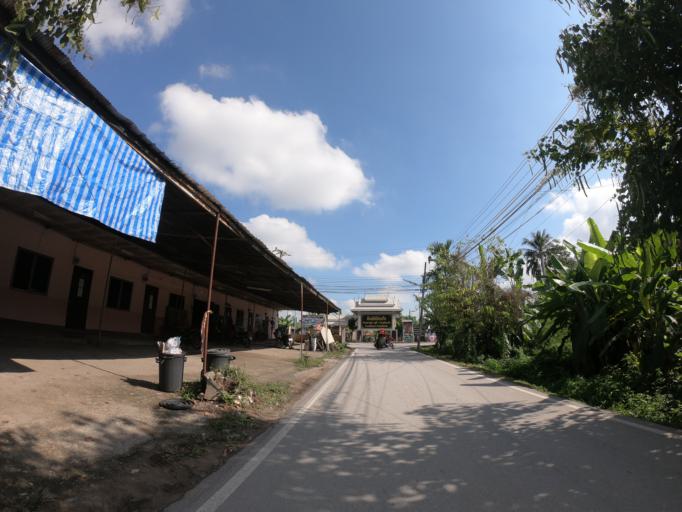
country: TH
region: Chiang Mai
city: San Sai
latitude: 18.8468
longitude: 99.0513
